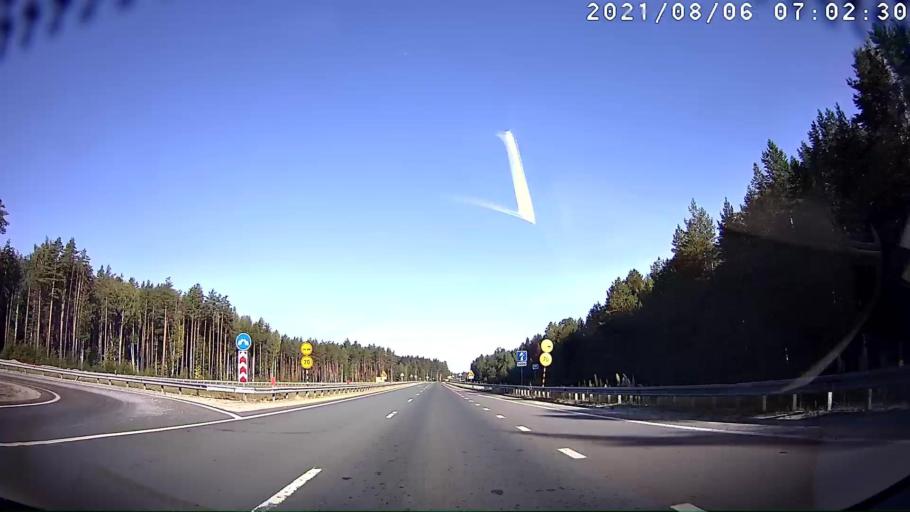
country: RU
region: Mariy-El
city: Yoshkar-Ola
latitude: 56.5347
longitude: 47.9952
